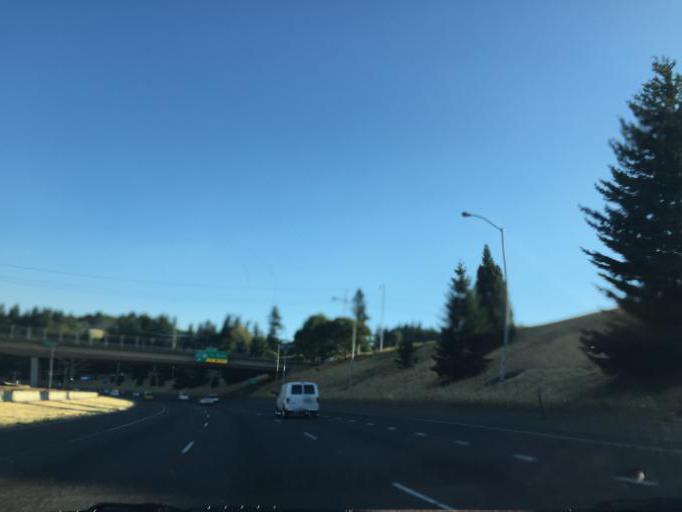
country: US
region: Oregon
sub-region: Multnomah County
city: Lents
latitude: 45.5568
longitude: -122.5673
